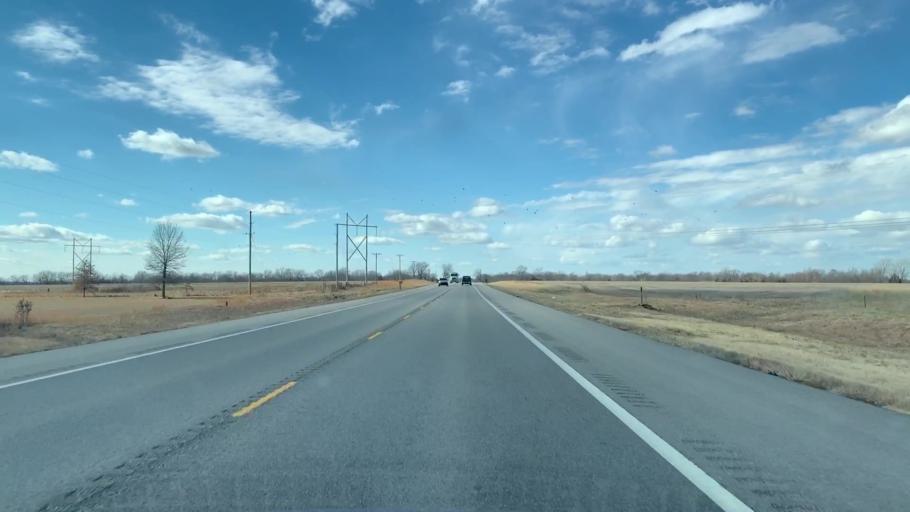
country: US
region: Kansas
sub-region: Labette County
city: Oswego
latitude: 37.3401
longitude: -95.0778
